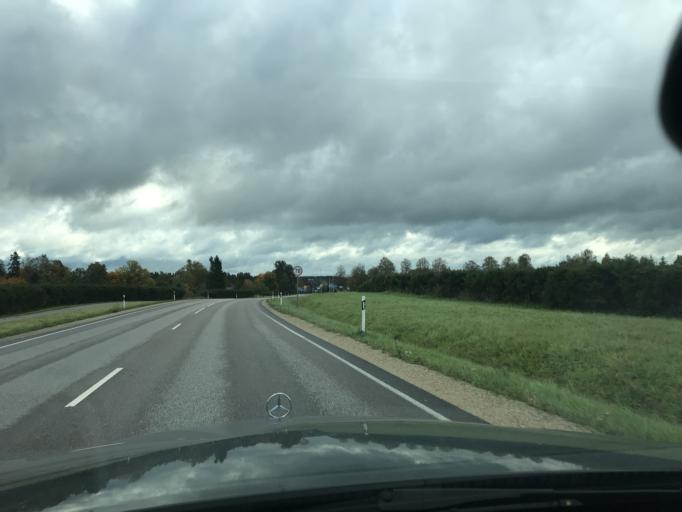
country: EE
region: Valgamaa
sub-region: Torva linn
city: Torva
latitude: 58.0084
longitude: 25.9072
